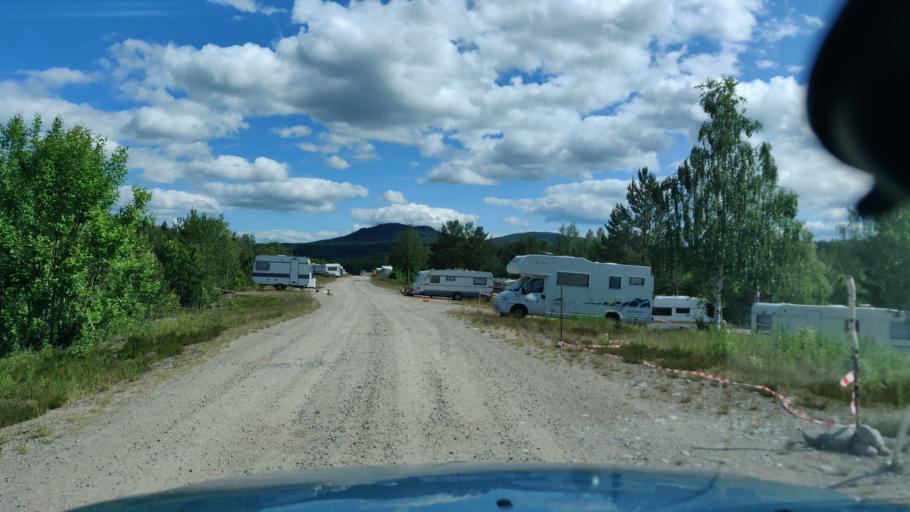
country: NO
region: Hedmark
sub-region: Trysil
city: Innbygda
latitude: 60.9116
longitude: 12.5622
